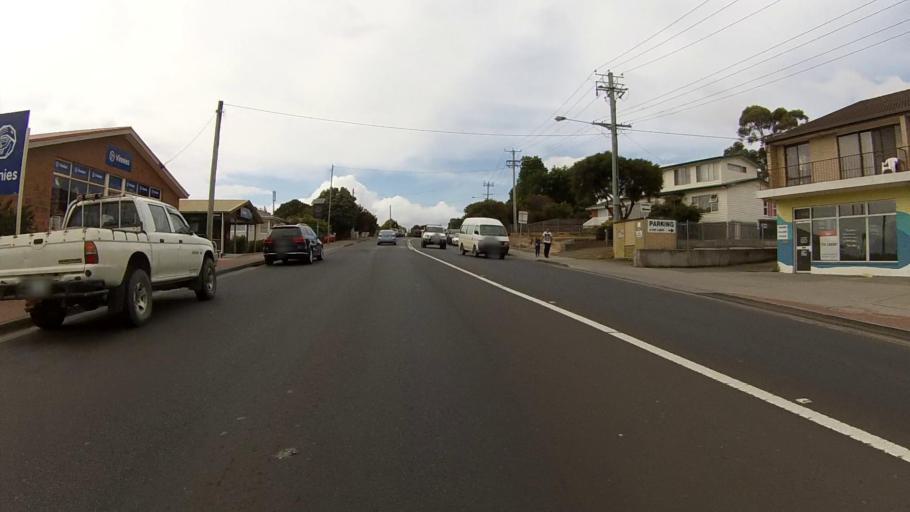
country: AU
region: Tasmania
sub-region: Kingborough
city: Margate
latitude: -43.0268
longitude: 147.2617
